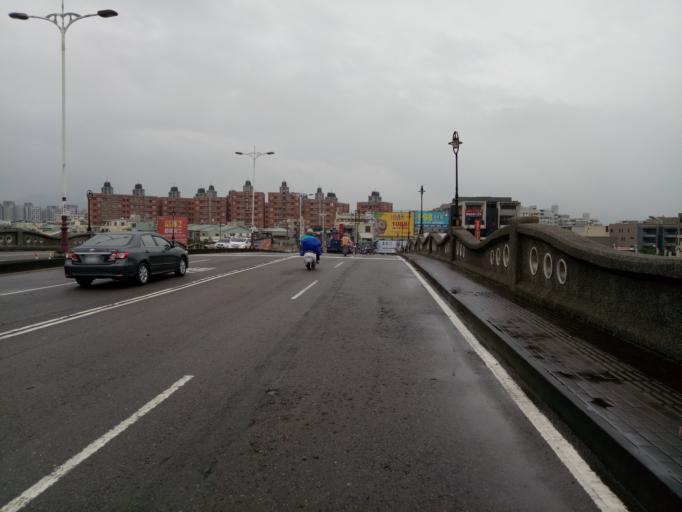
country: TW
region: Taiwan
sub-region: Taichung City
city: Taichung
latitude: 24.1106
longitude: 120.6980
